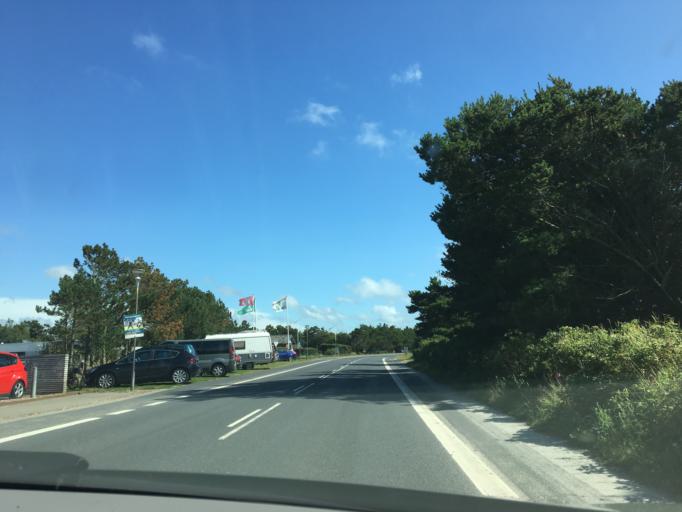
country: DK
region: South Denmark
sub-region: Varde Kommune
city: Oksbol
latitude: 55.7378
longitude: 8.1837
